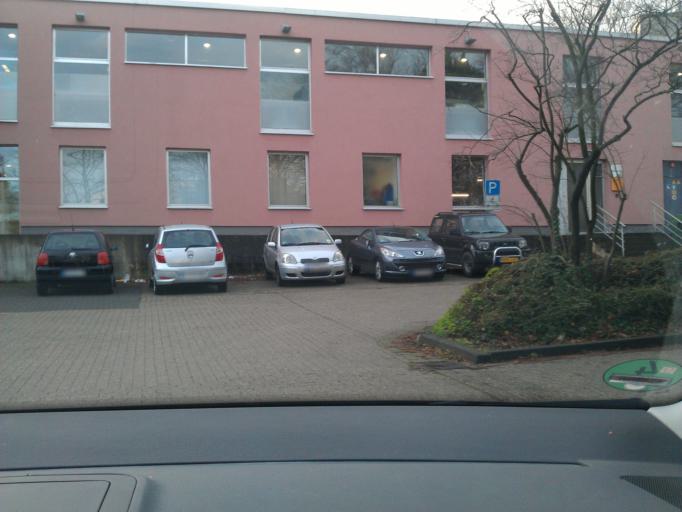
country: DE
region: North Rhine-Westphalia
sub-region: Regierungsbezirk Koln
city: Aachen
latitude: 50.7610
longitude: 6.0876
